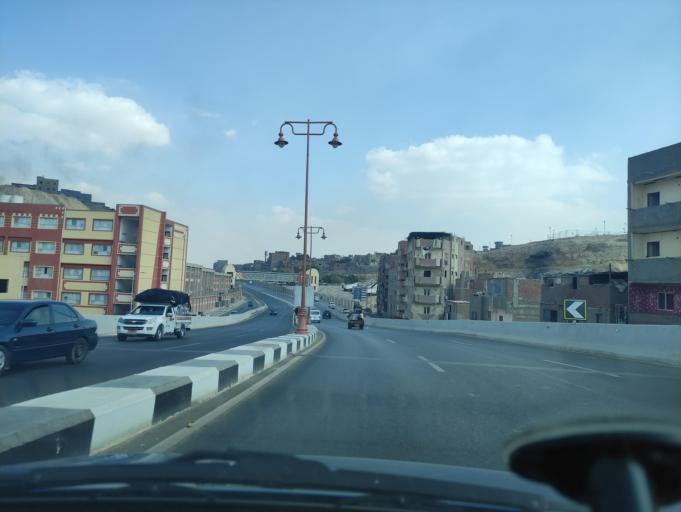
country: EG
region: Muhafazat al Qahirah
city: Cairo
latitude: 30.0475
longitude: 31.2872
